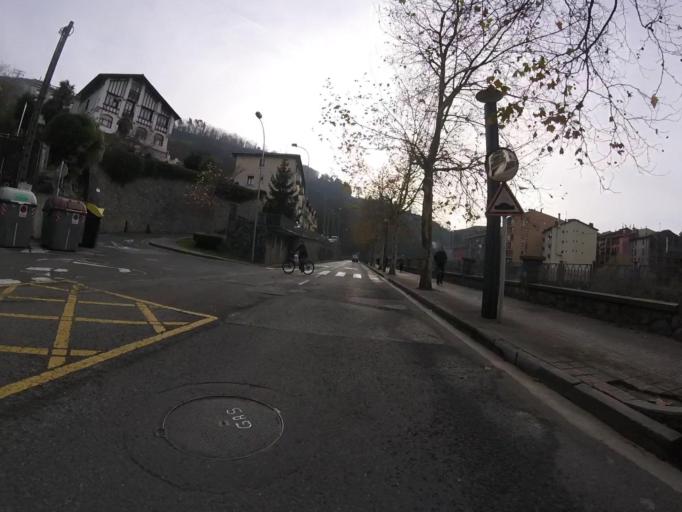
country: ES
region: Basque Country
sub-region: Provincia de Guipuzcoa
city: Tolosa
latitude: 43.1404
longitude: -2.0711
